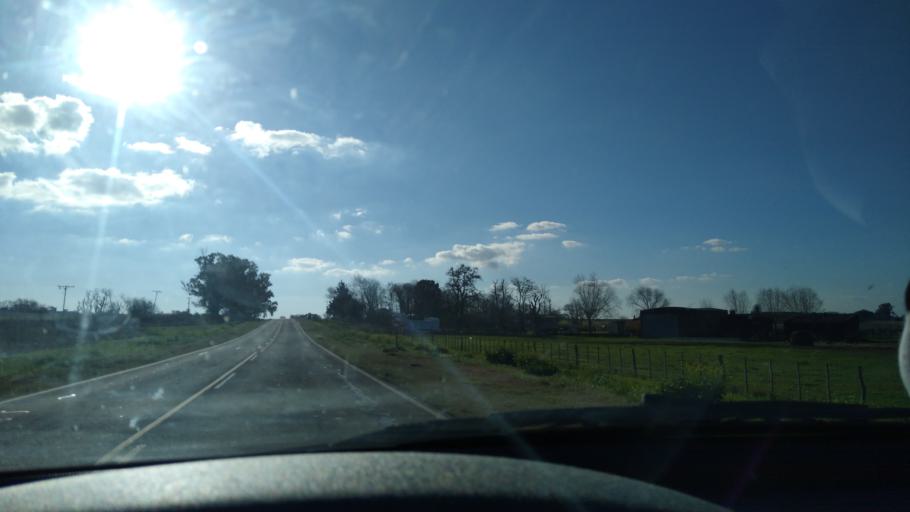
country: AR
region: Entre Rios
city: Diamante
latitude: -32.1148
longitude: -60.5731
